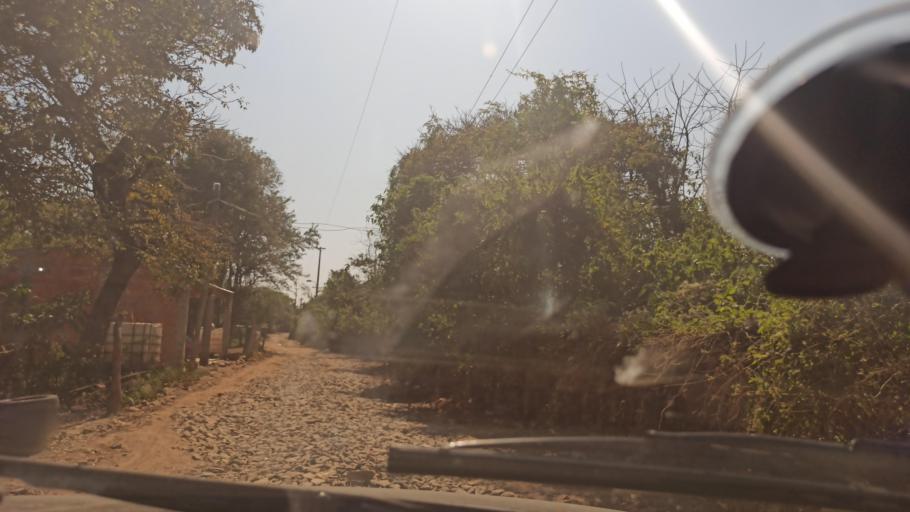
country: AR
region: Formosa
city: Clorinda
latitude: -25.3074
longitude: -57.6977
